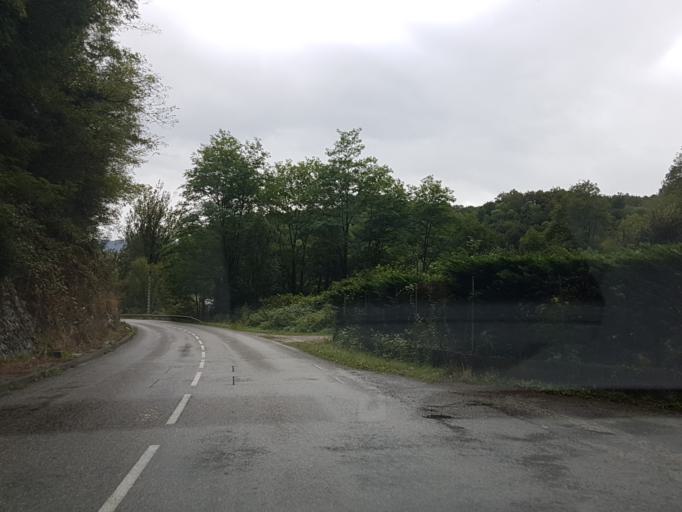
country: FR
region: Midi-Pyrenees
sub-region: Departement de l'Ariege
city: Saint-Girons
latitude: 42.9042
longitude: 1.2111
